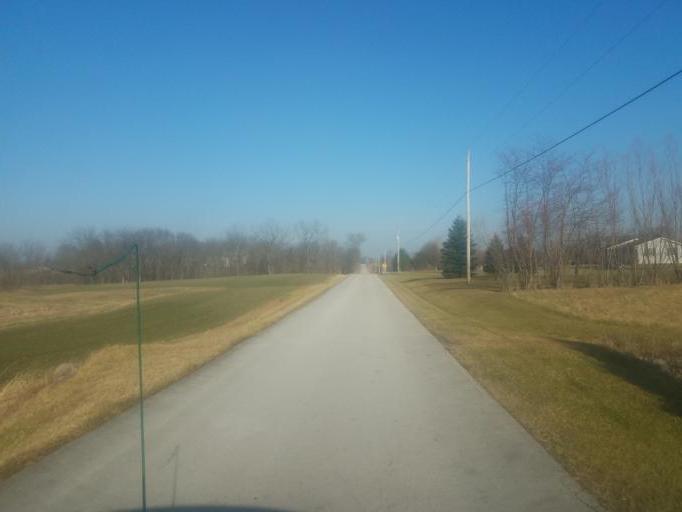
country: US
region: Ohio
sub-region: Seneca County
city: Tiffin
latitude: 41.0627
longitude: -83.1127
